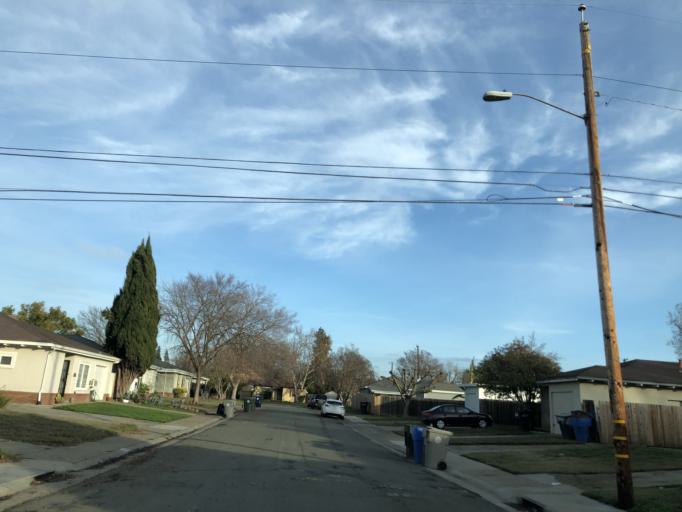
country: US
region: California
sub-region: Sacramento County
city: Parkway
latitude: 38.5513
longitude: -121.4353
